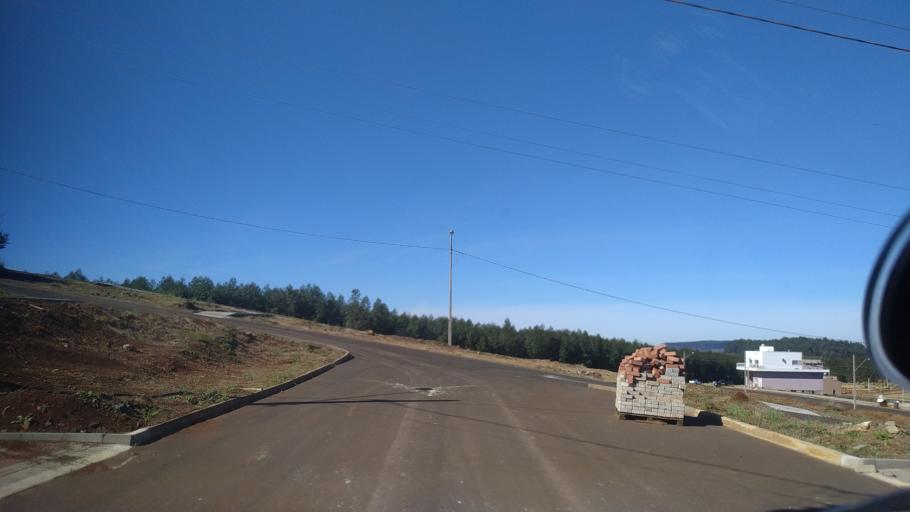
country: BR
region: Santa Catarina
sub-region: Chapeco
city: Chapeco
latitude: -27.0531
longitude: -52.5942
